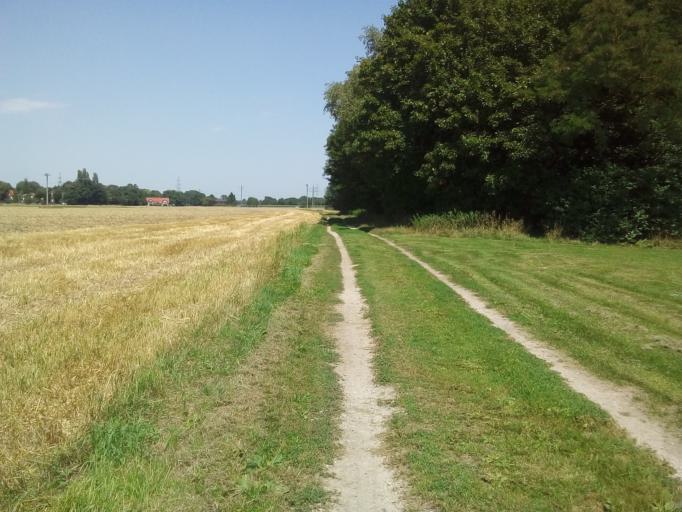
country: DE
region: Bavaria
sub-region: Upper Bavaria
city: Unterfoehring
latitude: 48.1630
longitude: 11.6527
